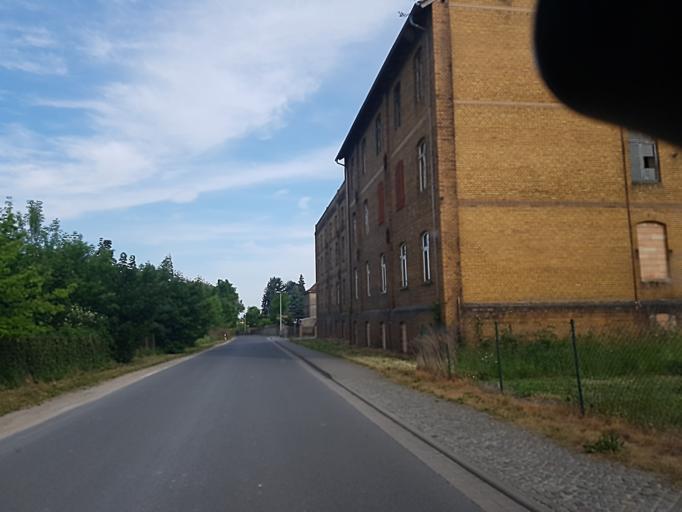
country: DE
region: Saxony-Anhalt
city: Zahna
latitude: 51.9172
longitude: 12.7734
